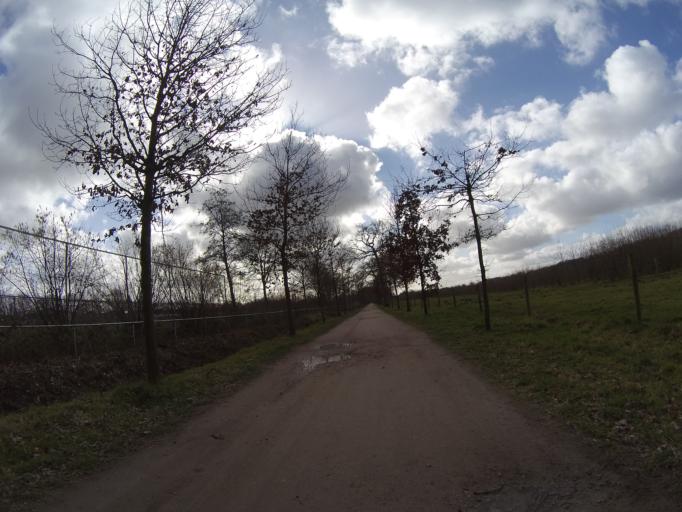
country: NL
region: Gelderland
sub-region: Gemeente Nijkerk
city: Nijkerk
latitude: 52.1819
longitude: 5.4502
